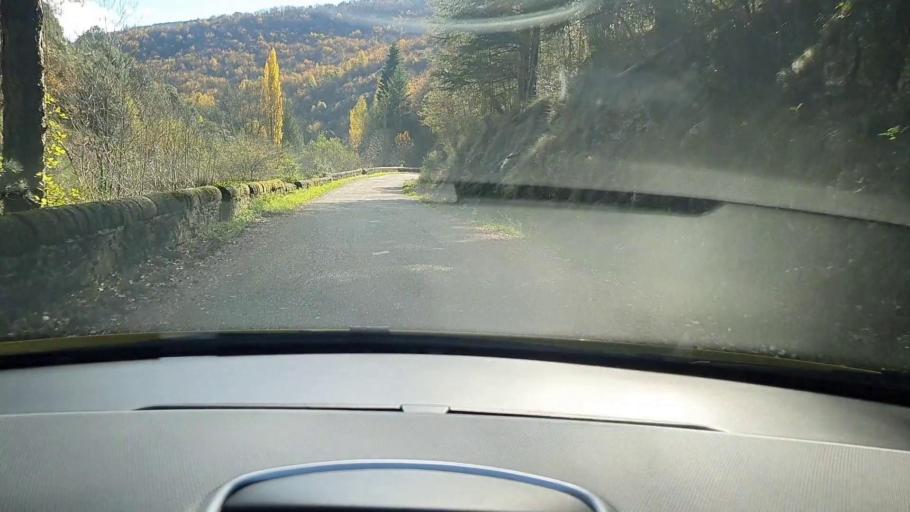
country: FR
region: Languedoc-Roussillon
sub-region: Departement du Gard
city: Valleraugue
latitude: 44.1731
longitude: 3.6452
